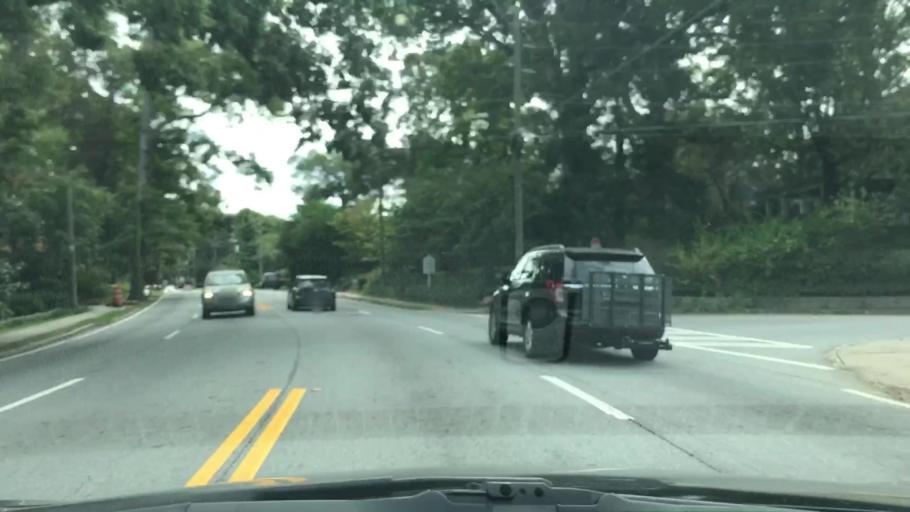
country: US
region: Georgia
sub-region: DeKalb County
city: North Decatur
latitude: 33.7869
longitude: -84.3065
